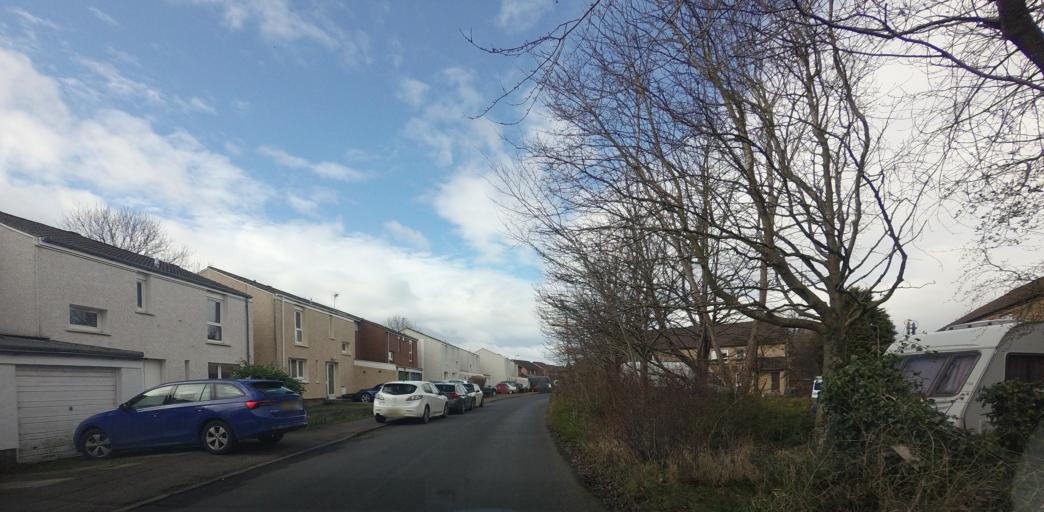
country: GB
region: Scotland
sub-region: Edinburgh
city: Queensferry
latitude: 55.9910
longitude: -3.4126
